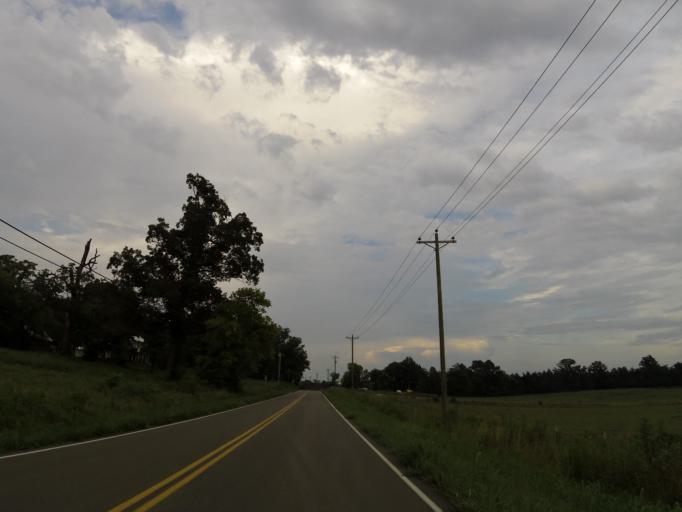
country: US
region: Tennessee
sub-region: Loudon County
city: Greenback
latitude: 35.6491
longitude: -84.1948
